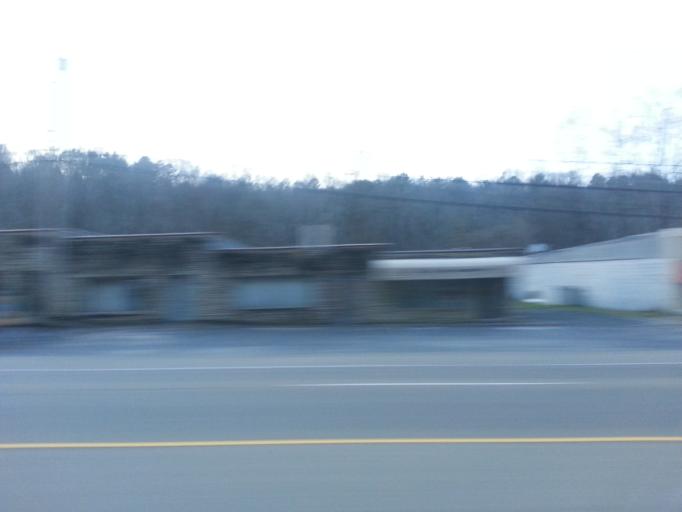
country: US
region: Tennessee
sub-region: Roane County
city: Harriman
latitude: 35.9263
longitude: -84.5585
